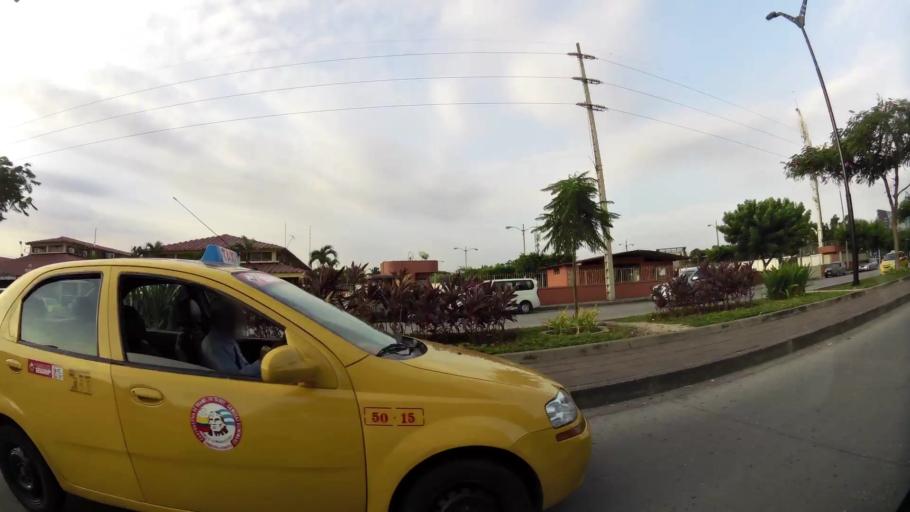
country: EC
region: Guayas
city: Eloy Alfaro
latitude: -2.1448
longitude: -79.8836
